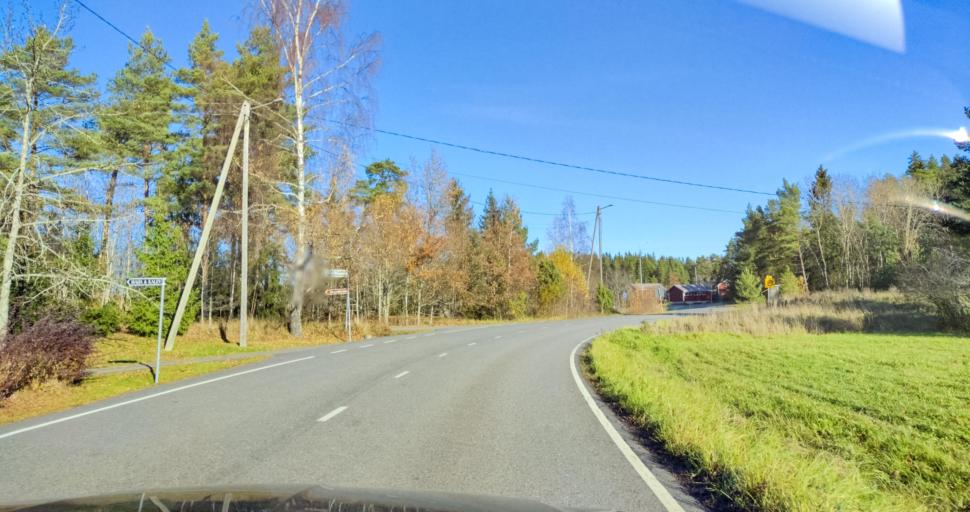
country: FI
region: Varsinais-Suomi
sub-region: Turku
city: Turku
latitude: 60.4036
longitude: 22.2093
